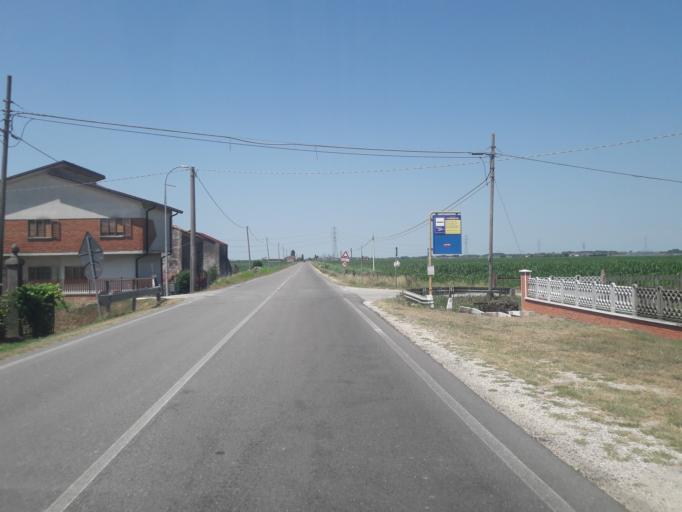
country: IT
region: Veneto
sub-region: Provincia di Rovigo
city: Papozze
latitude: 45.0049
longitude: 12.1818
